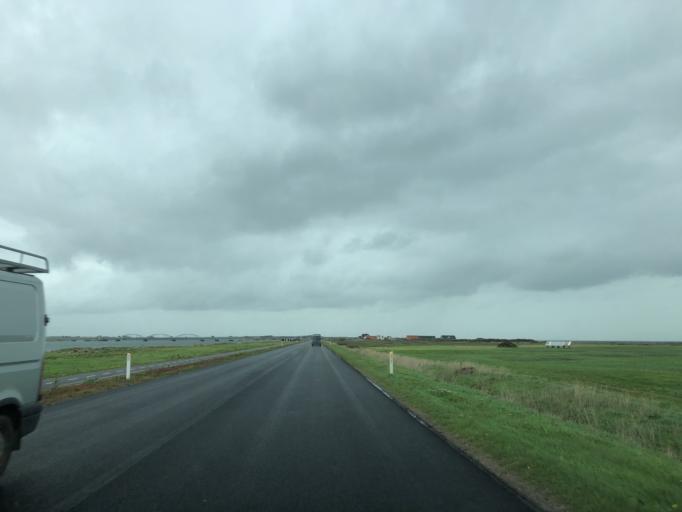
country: DK
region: Central Jutland
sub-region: Struer Kommune
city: Struer
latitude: 56.5652
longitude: 8.5592
